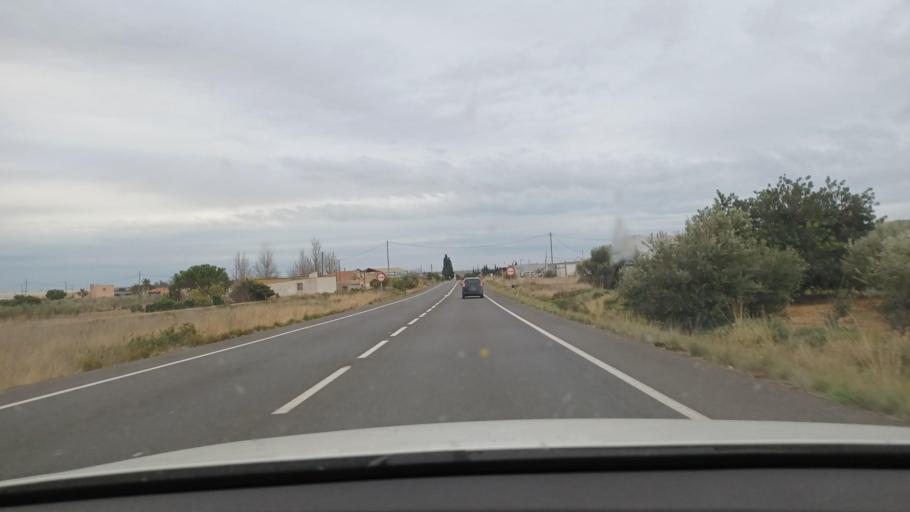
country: ES
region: Catalonia
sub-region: Provincia de Tarragona
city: Amposta
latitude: 40.6990
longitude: 0.5691
